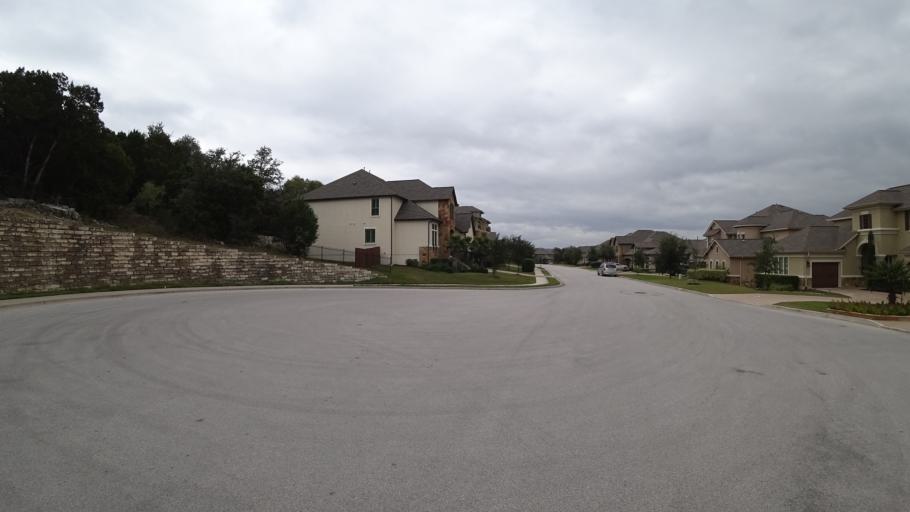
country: US
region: Texas
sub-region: Travis County
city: Bee Cave
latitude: 30.3428
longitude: -97.9122
